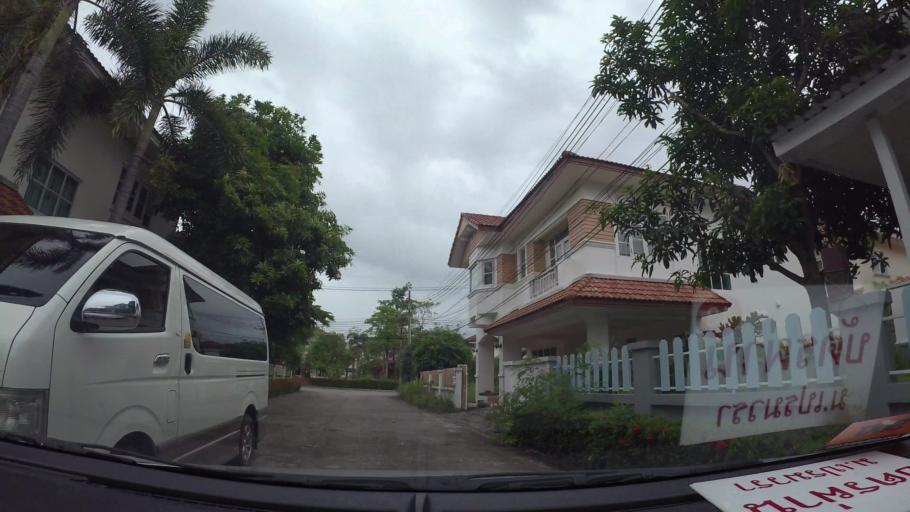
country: TH
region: Chon Buri
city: Si Racha
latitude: 13.1491
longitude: 100.9789
